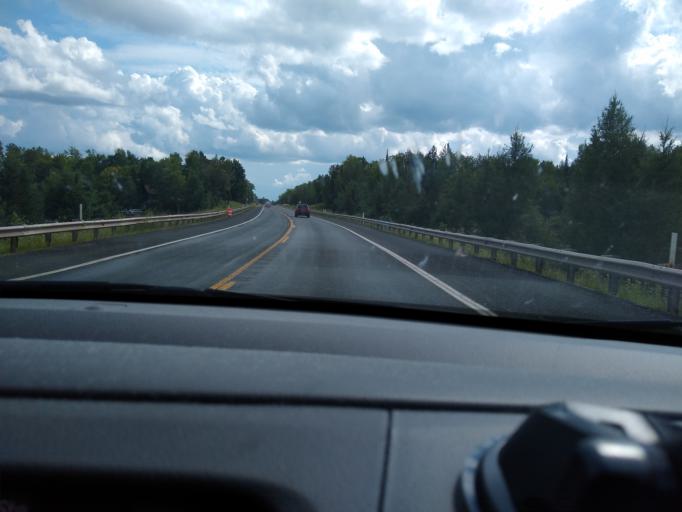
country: US
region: Michigan
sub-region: Iron County
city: Crystal Falls
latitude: 46.2810
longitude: -88.0180
